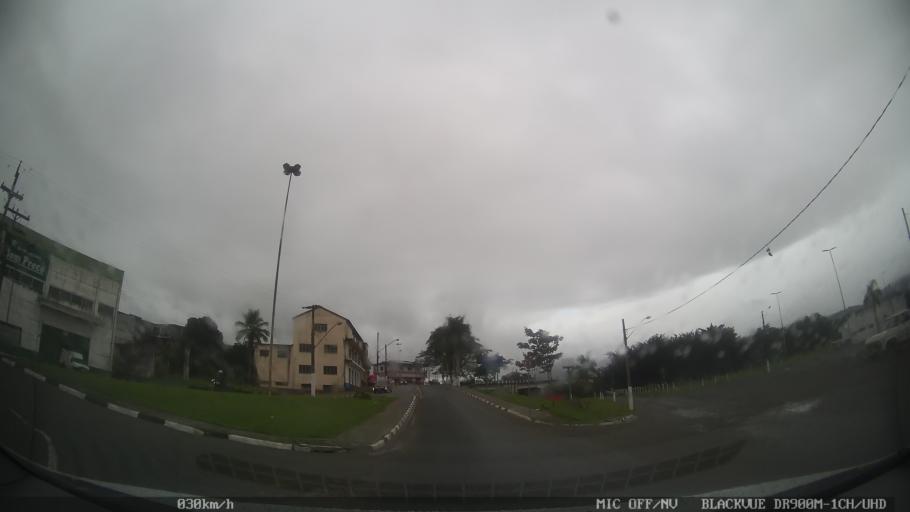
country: BR
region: Sao Paulo
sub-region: Juquia
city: Juquia
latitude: -24.3218
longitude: -47.6373
